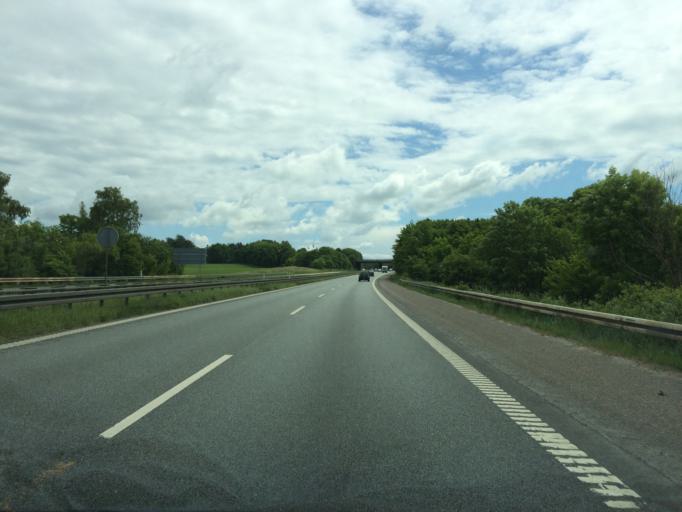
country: DK
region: Zealand
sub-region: Lejre Kommune
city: Lejre
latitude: 55.6470
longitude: 11.9315
